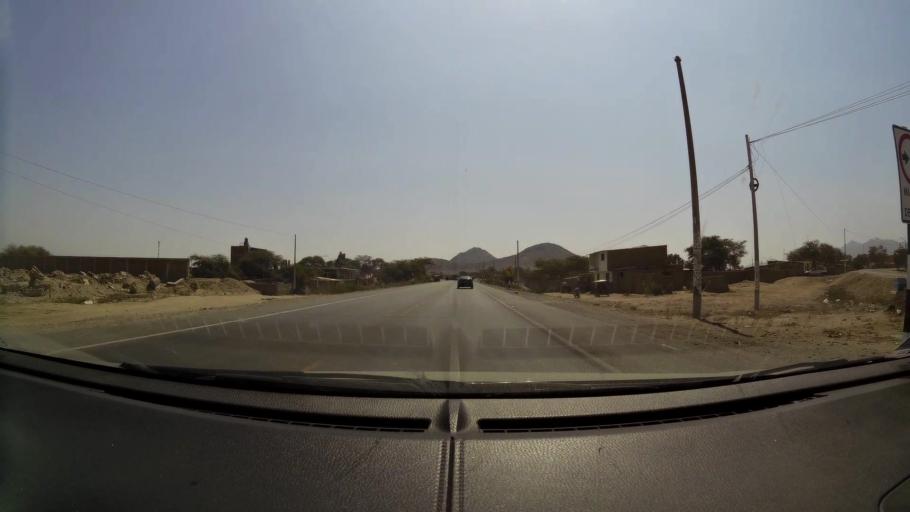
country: PE
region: Lambayeque
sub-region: Provincia de Chiclayo
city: Mocupe
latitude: -6.9800
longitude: -79.6428
